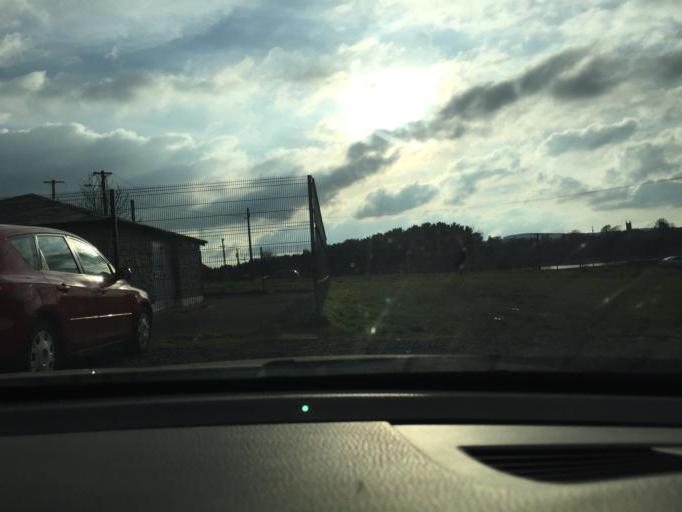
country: IE
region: Leinster
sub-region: Wicklow
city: Blessington
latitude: 53.1694
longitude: -6.5177
